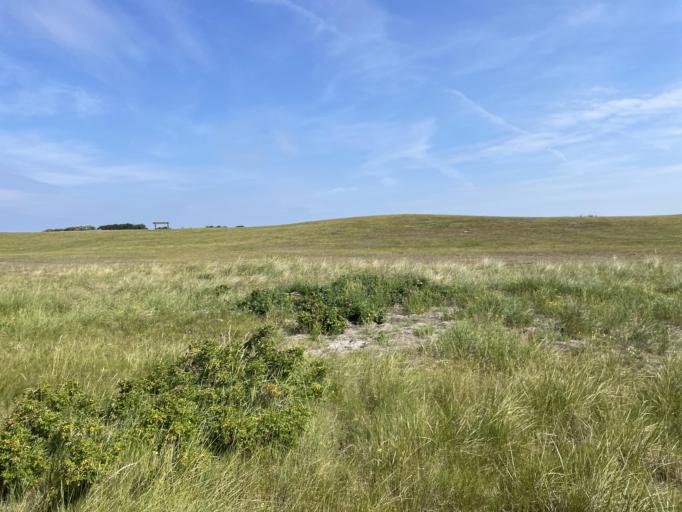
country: DE
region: Lower Saxony
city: Wangerooge
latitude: 53.7880
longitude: 7.8834
